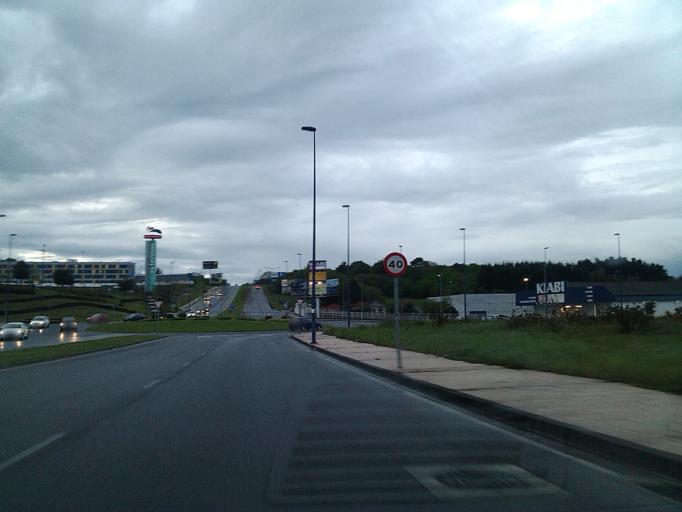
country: ES
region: Galicia
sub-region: Provincia de Lugo
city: Lugo
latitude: 43.0359
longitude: -7.5654
